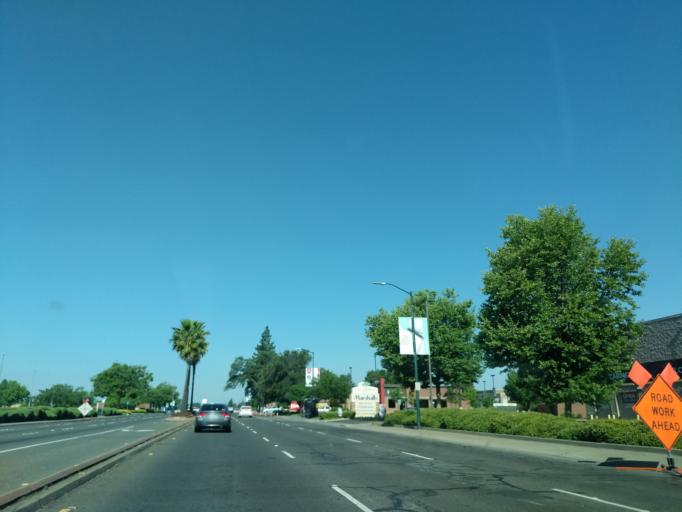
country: US
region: California
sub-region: Sacramento County
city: Citrus Heights
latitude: 38.6785
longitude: -121.2674
